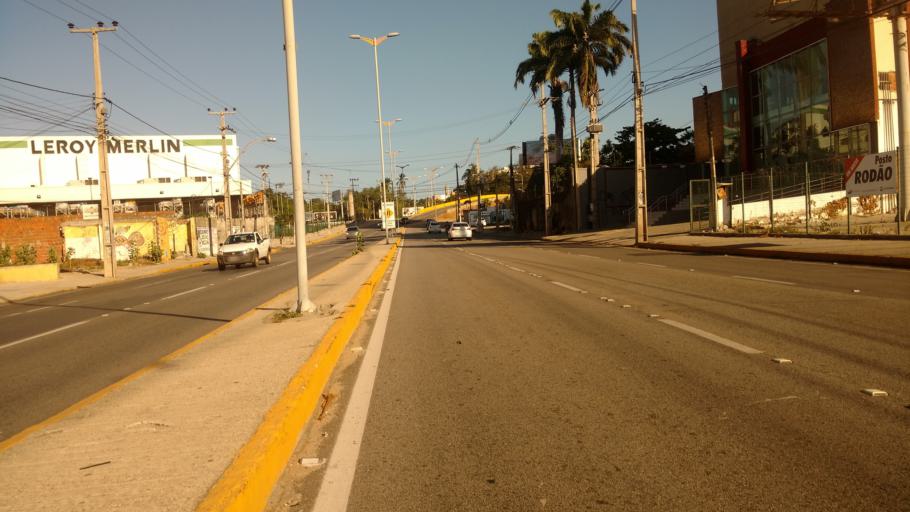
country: BR
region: Ceara
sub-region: Fortaleza
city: Fortaleza
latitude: -3.7584
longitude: -38.4856
